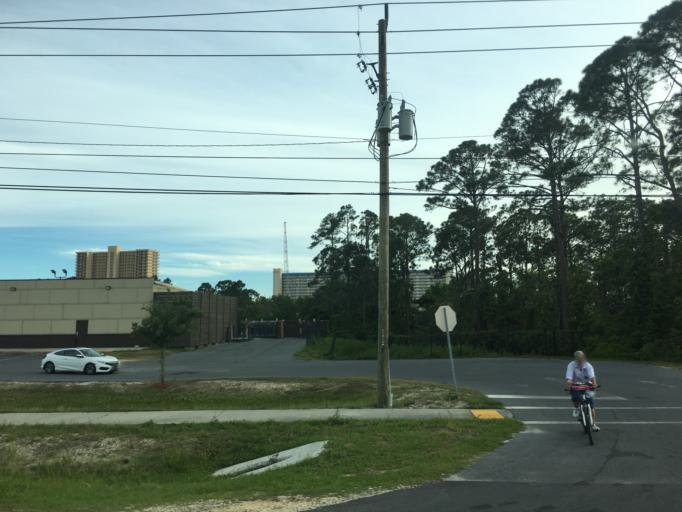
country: US
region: Florida
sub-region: Bay County
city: Panama City Beach
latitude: 30.1724
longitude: -85.7903
